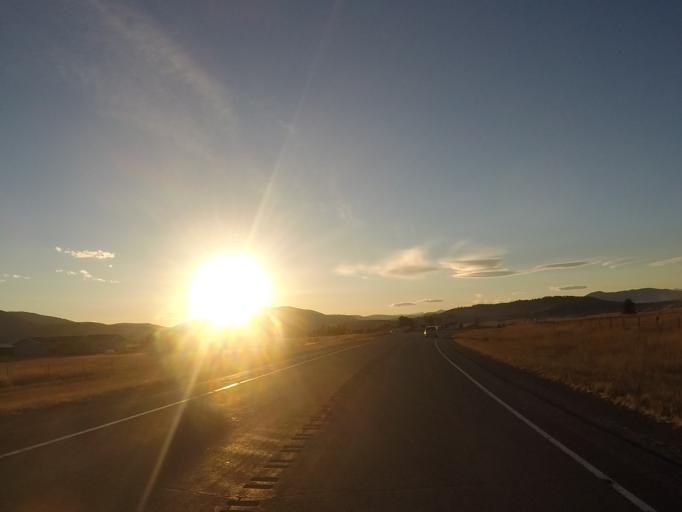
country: US
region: Montana
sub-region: Missoula County
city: Seeley Lake
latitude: 47.0201
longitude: -113.1184
